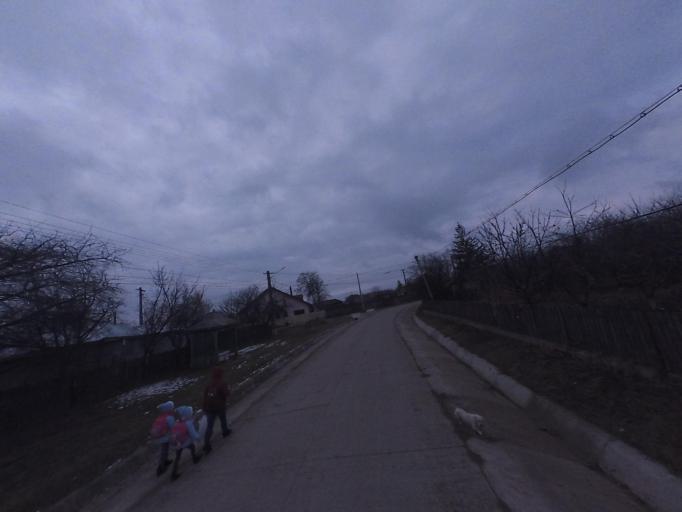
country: RO
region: Iasi
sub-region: Comuna Popricani
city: Popricani
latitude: 47.2902
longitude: 27.5080
